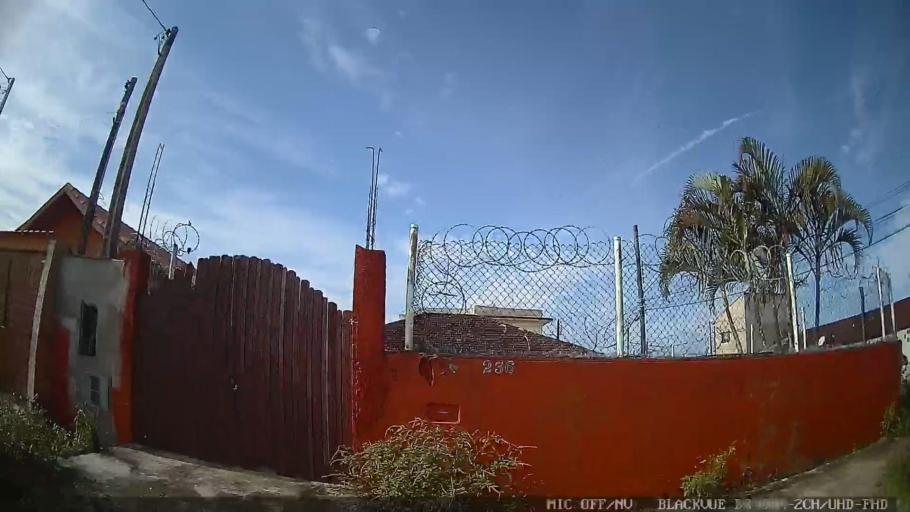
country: BR
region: Sao Paulo
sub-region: Itanhaem
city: Itanhaem
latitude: -24.1640
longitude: -46.7657
